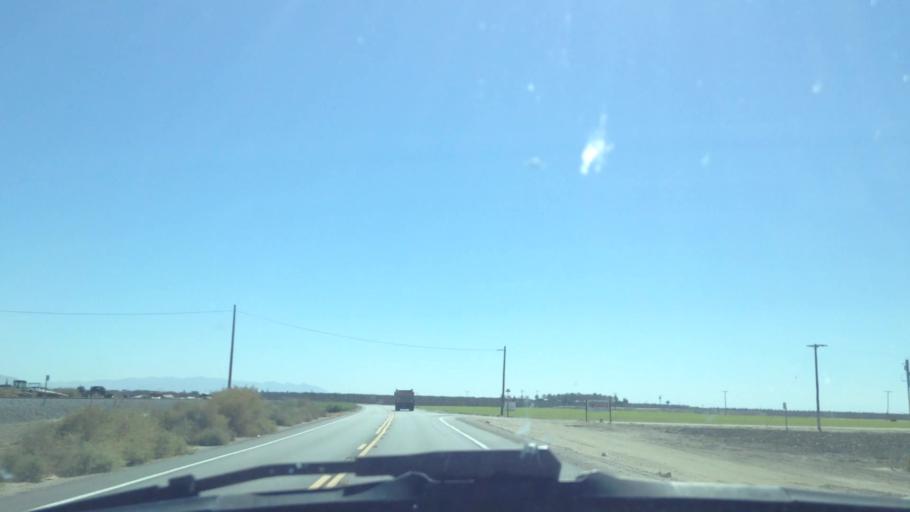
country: US
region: California
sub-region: Riverside County
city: Mecca
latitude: 33.5392
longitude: -116.0275
